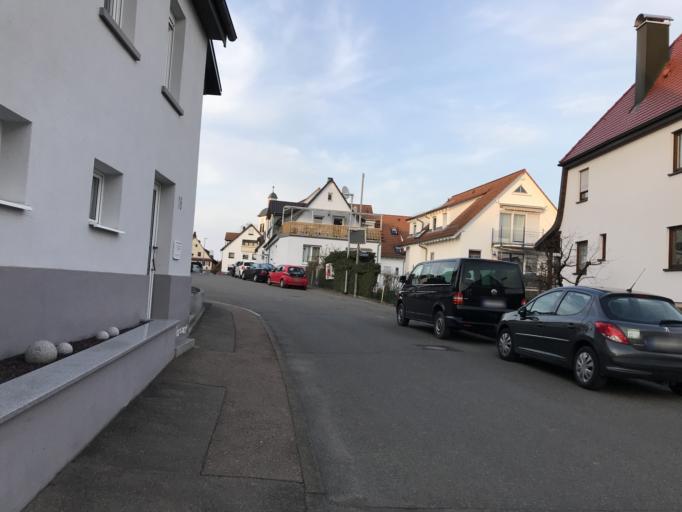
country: DE
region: Baden-Wuerttemberg
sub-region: Regierungsbezirk Stuttgart
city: Unterensingen
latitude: 48.6544
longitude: 9.3512
